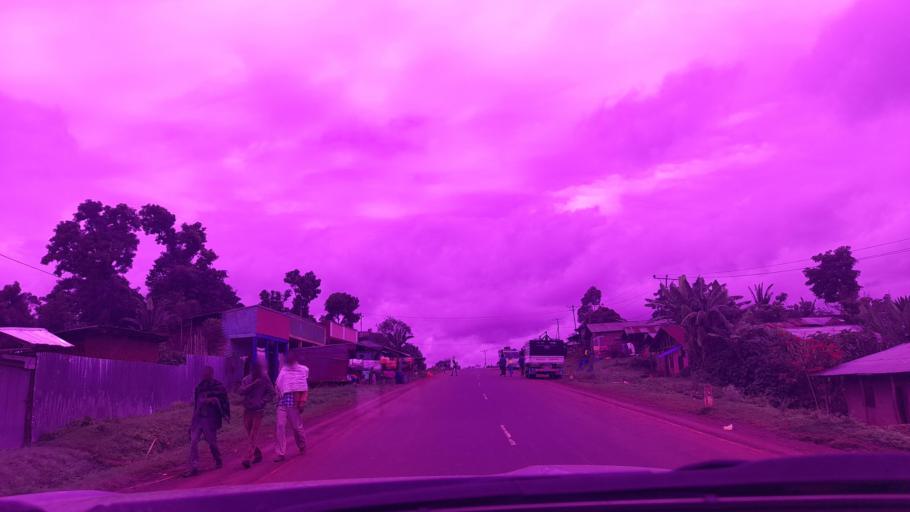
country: ET
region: Southern Nations, Nationalities, and People's Region
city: Bonga
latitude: 7.2974
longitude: 35.9883
